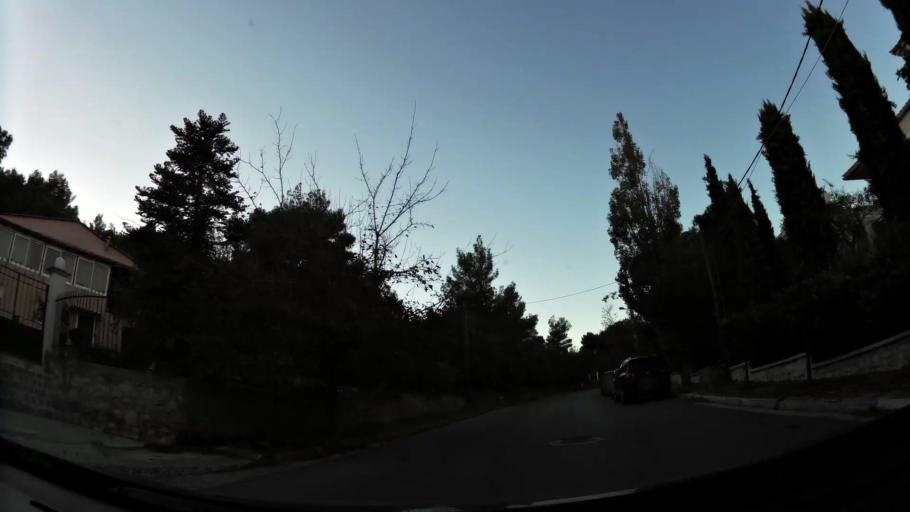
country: GR
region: Attica
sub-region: Nomarchia Athinas
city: Nea Penteli
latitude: 38.0501
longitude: 23.8518
